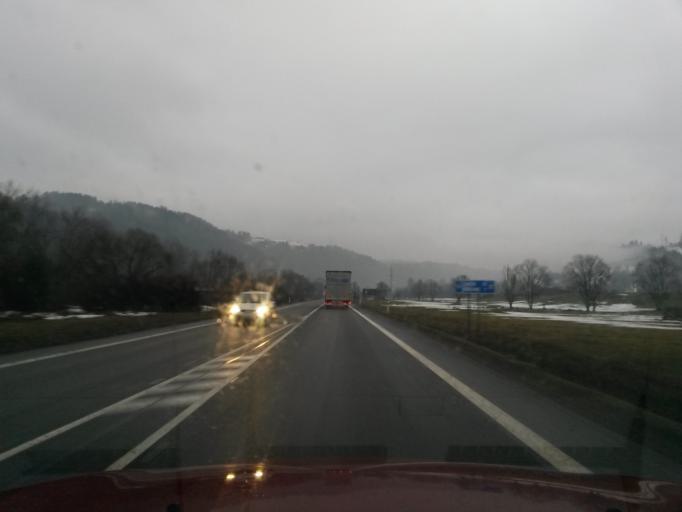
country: SK
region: Zilinsky
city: Kysucke Nove Mesto
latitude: 49.3445
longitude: 18.8102
